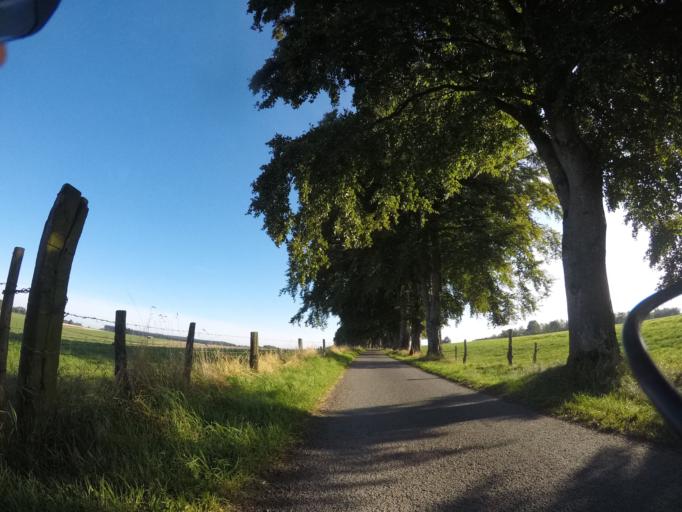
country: BE
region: Wallonia
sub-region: Province du Luxembourg
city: Bastogne
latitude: 49.9629
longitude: 5.7114
